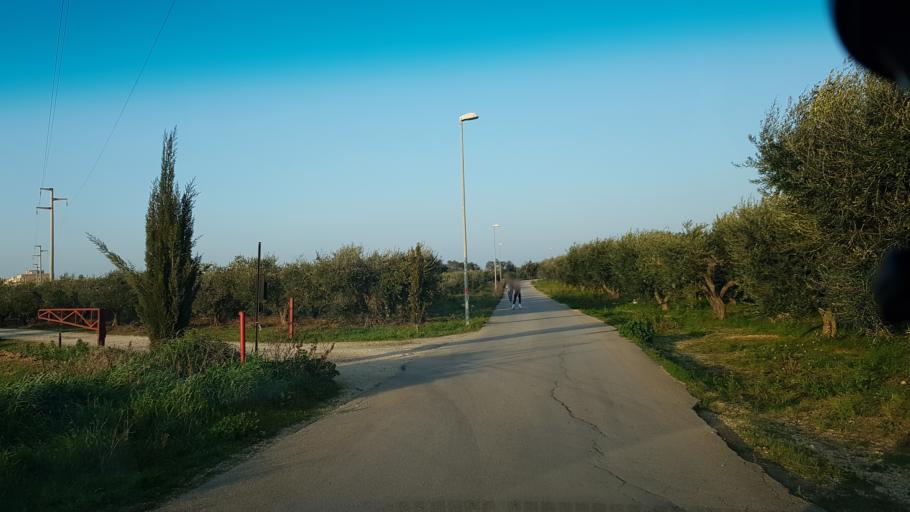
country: IT
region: Apulia
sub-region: Provincia di Brindisi
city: Mesagne
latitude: 40.5525
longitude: 17.7948
